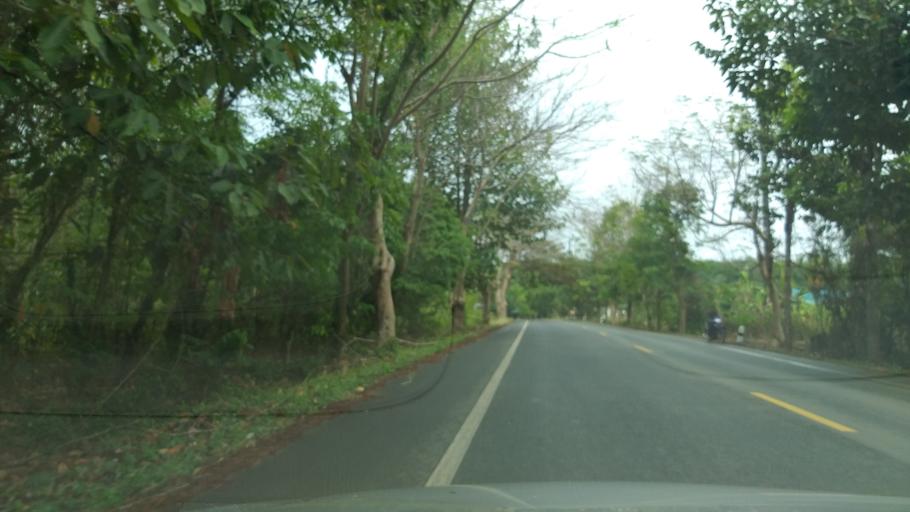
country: TH
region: Trat
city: Khao Saming
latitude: 12.3247
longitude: 102.3665
